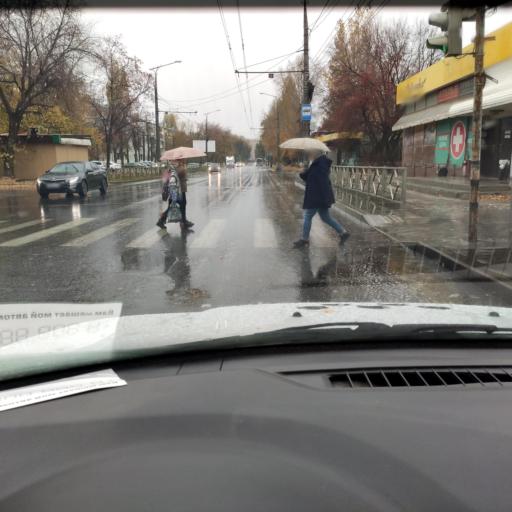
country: RU
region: Samara
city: Tol'yatti
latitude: 53.5121
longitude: 49.4300
